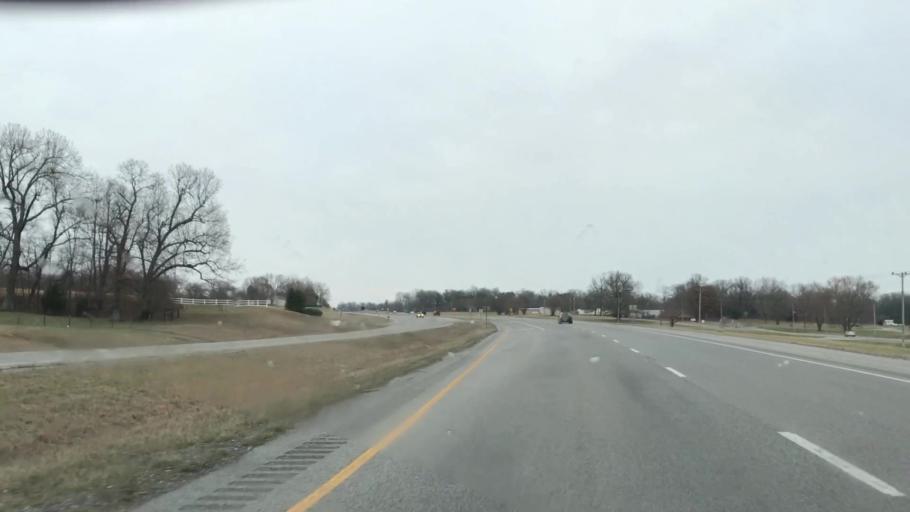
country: US
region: Kentucky
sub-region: Trigg County
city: Cadiz
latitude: 36.8648
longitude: -87.7805
